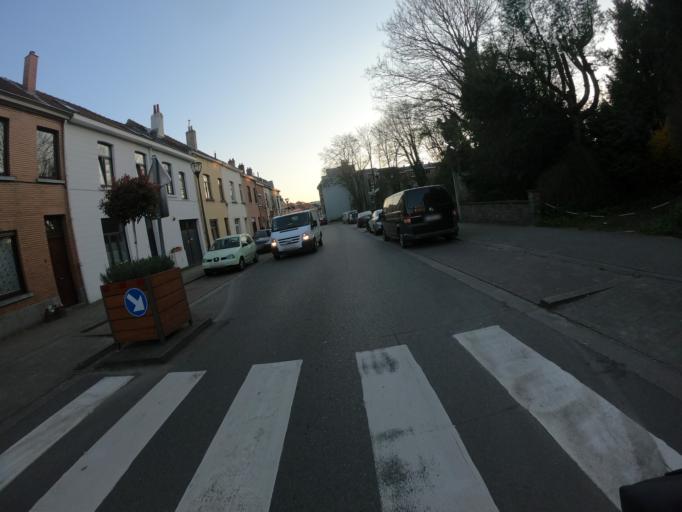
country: BE
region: Flanders
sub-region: Provincie Vlaams-Brabant
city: Kraainem
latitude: 50.8500
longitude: 4.4324
